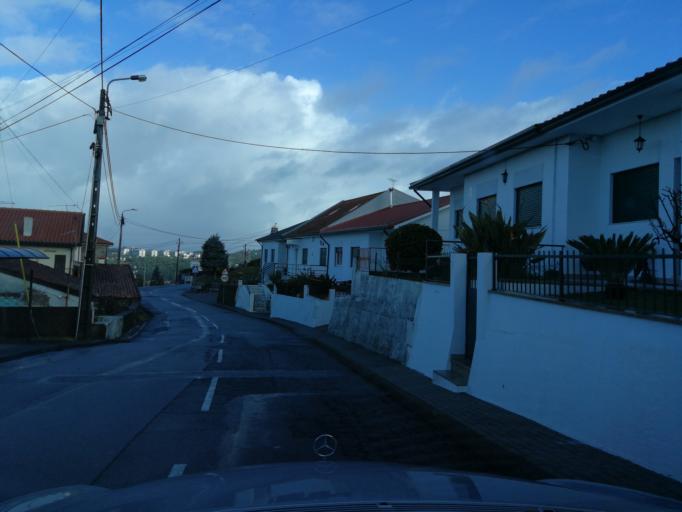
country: PT
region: Braga
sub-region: Braga
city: Braga
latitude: 41.5499
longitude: -8.3883
